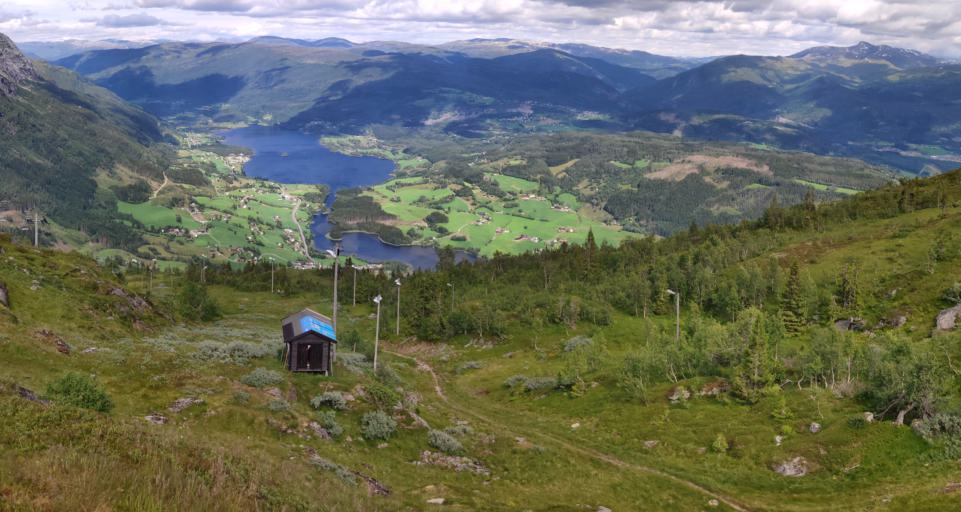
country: NO
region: Hordaland
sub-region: Voss
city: Voss
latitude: 60.6466
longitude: 6.4035
